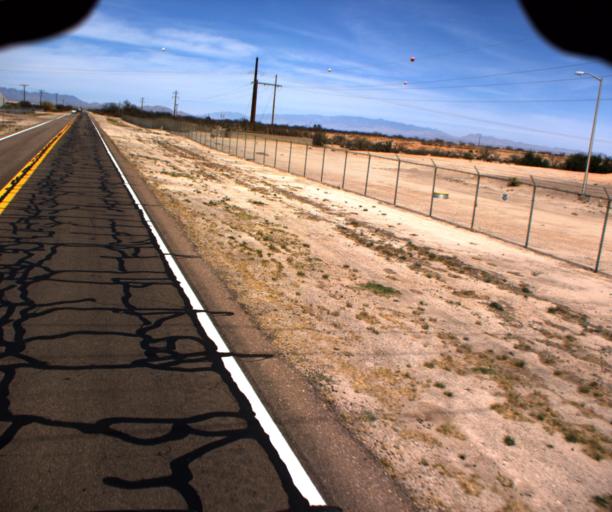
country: US
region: Arizona
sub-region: Cochise County
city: Willcox
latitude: 32.0624
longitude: -109.8922
